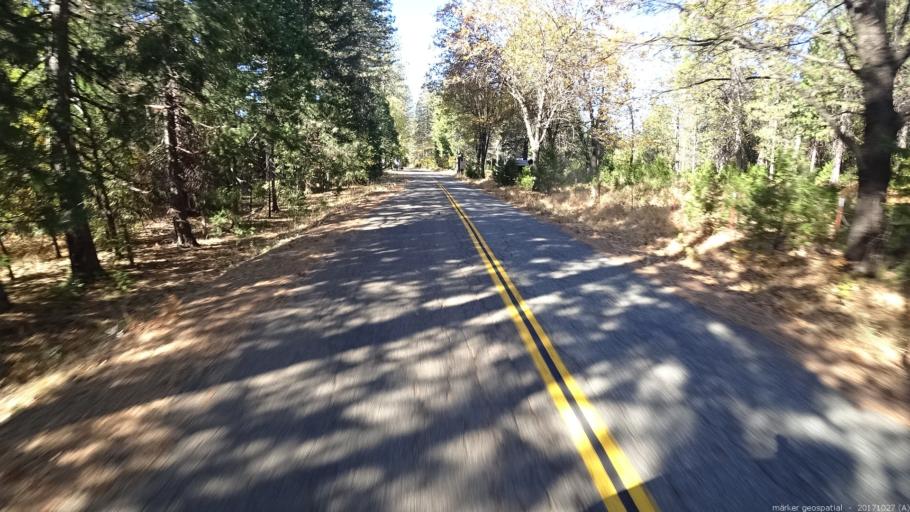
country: US
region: California
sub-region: Shasta County
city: Burney
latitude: 40.8262
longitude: -121.9494
